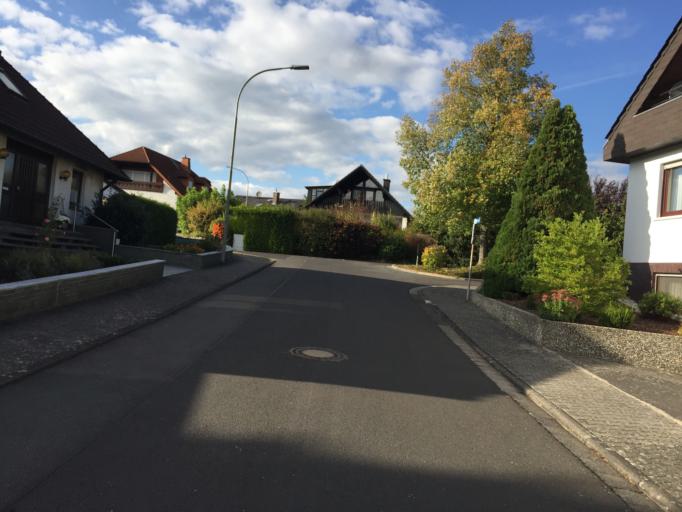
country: DE
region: Hesse
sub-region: Regierungsbezirk Darmstadt
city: Rockenberg
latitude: 50.4649
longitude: 8.7358
